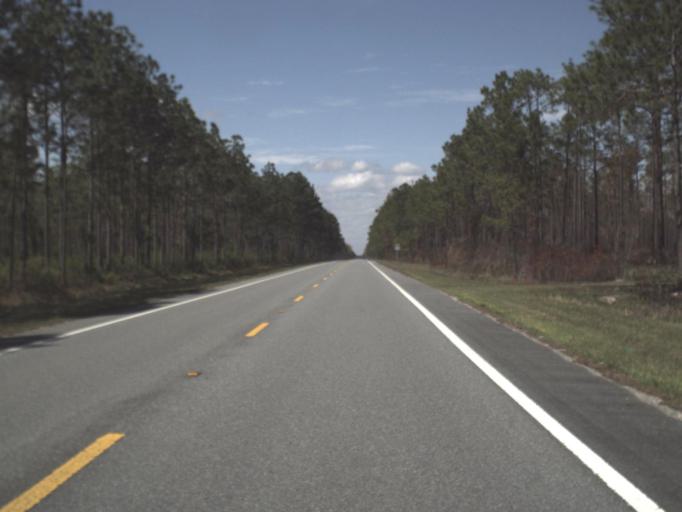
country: US
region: Florida
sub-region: Gadsden County
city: Midway
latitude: 30.3634
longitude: -84.5377
